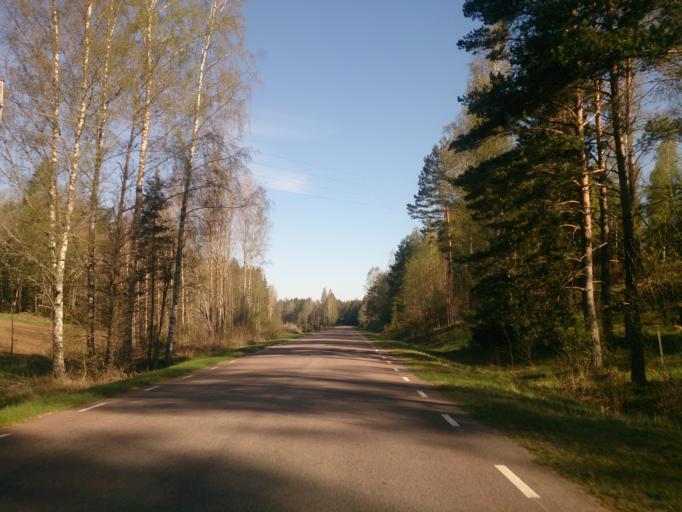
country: SE
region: OEstergoetland
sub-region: Linkopings Kommun
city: Ljungsbro
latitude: 58.6097
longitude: 15.4776
